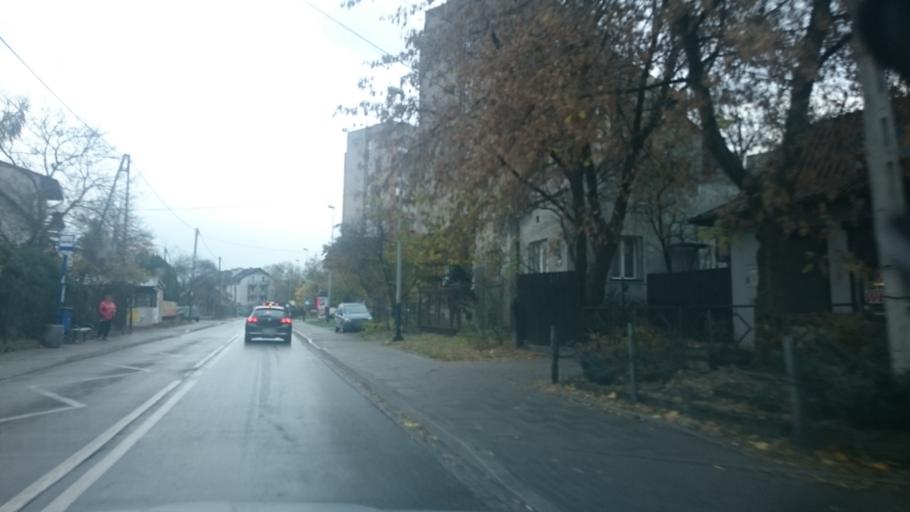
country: PL
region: Lesser Poland Voivodeship
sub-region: Krakow
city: Krakow
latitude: 50.0238
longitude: 19.9963
